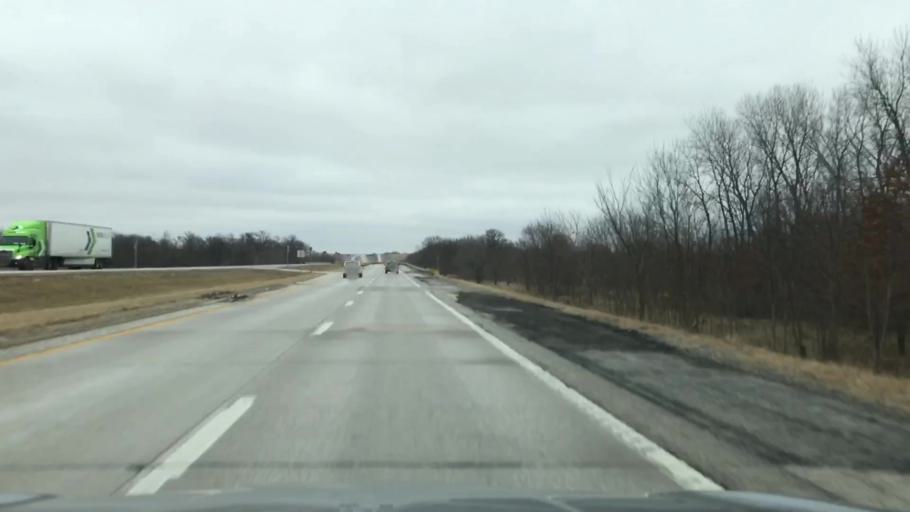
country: US
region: Missouri
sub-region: Linn County
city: Marceline
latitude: 39.7613
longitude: -92.9808
